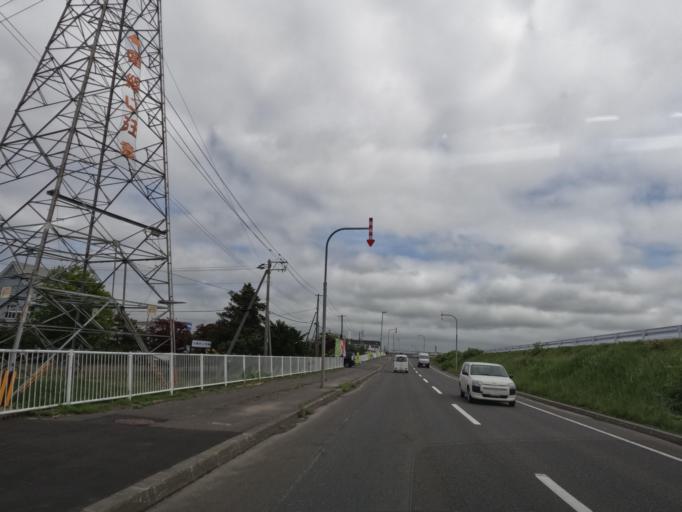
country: JP
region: Hokkaido
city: Sapporo
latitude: 43.0824
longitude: 141.4129
